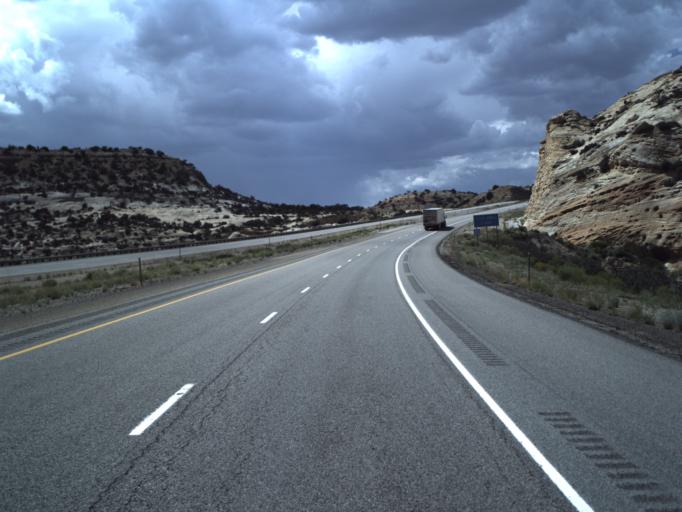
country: US
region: Utah
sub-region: Emery County
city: Ferron
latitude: 38.8471
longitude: -110.8936
